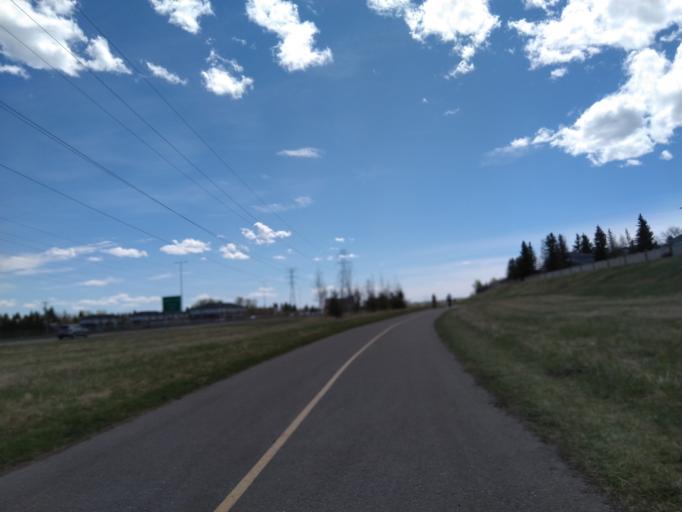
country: CA
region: Alberta
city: Calgary
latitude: 51.0281
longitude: -114.1649
